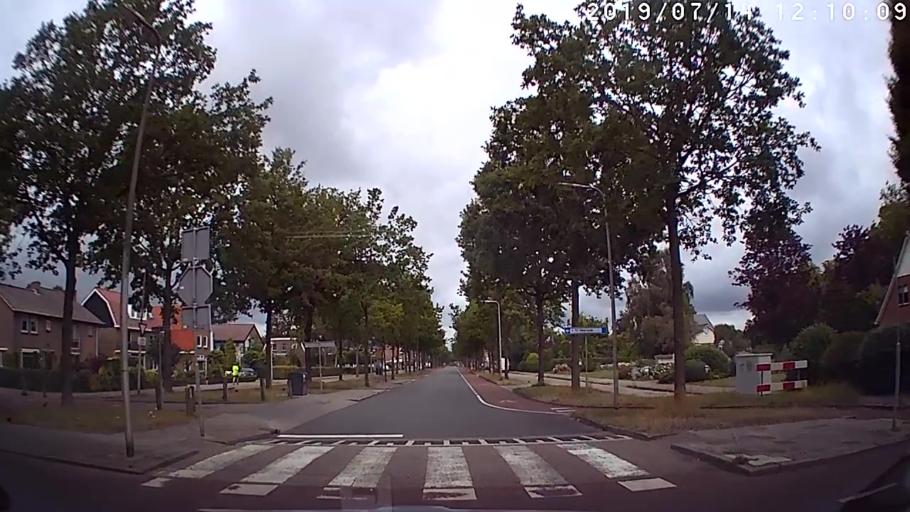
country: NL
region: Overijssel
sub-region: Gemeente Zwolle
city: Zwolle
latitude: 52.4863
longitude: 6.1130
